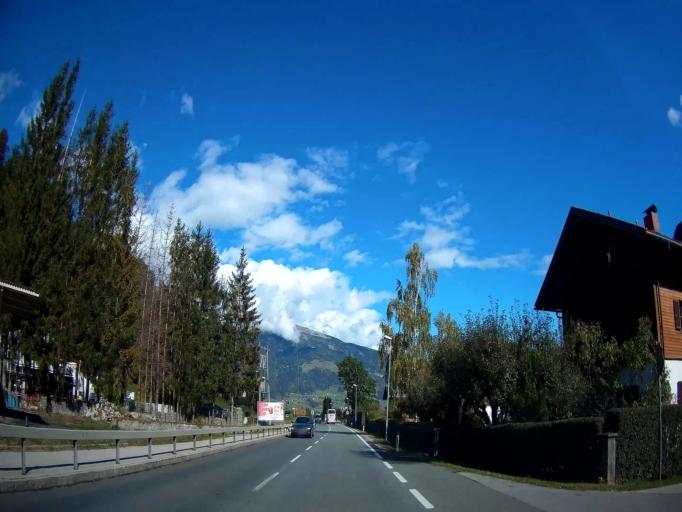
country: AT
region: Tyrol
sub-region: Politischer Bezirk Lienz
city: Leisach
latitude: 46.8036
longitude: 12.7459
